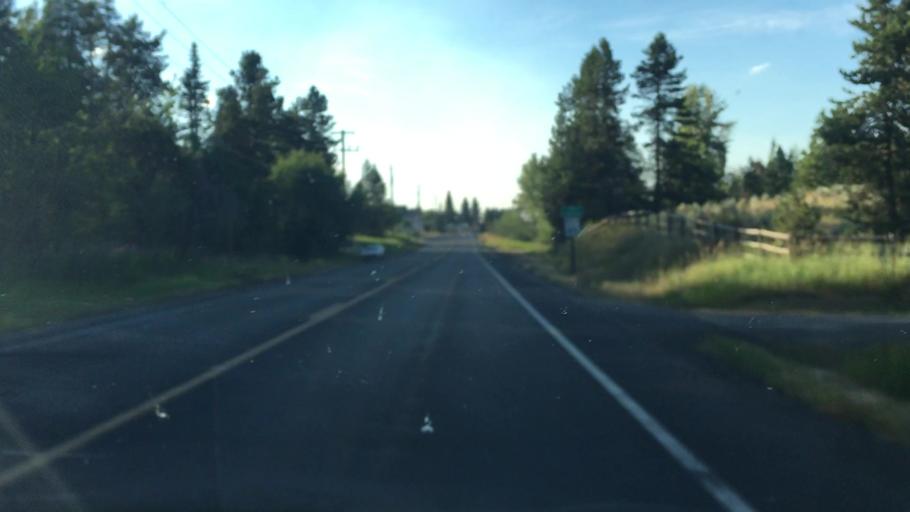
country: US
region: Idaho
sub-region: Valley County
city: McCall
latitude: 44.8292
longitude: -116.0822
